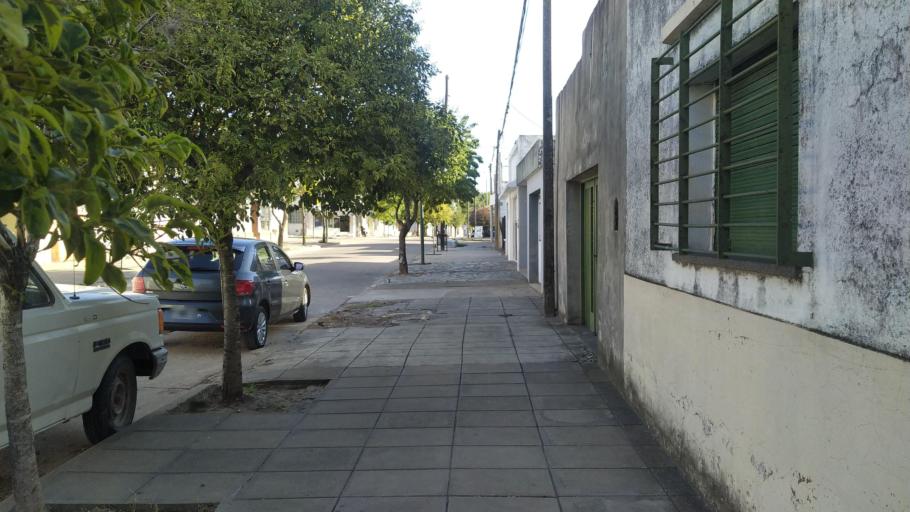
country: AR
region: Buenos Aires
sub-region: Partido de Salto
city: Salto
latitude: -34.2880
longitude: -60.2576
